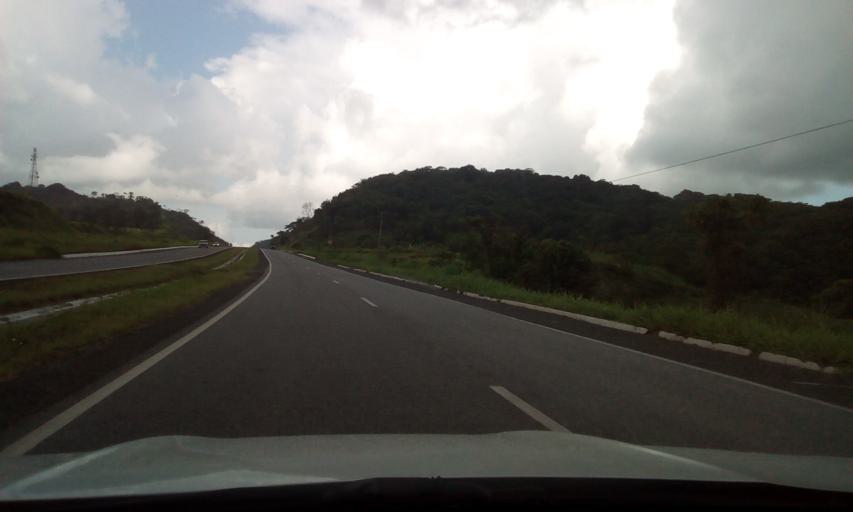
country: BR
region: Pernambuco
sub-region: Cabo De Santo Agostinho
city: Cabo
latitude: -8.2598
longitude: -35.0461
